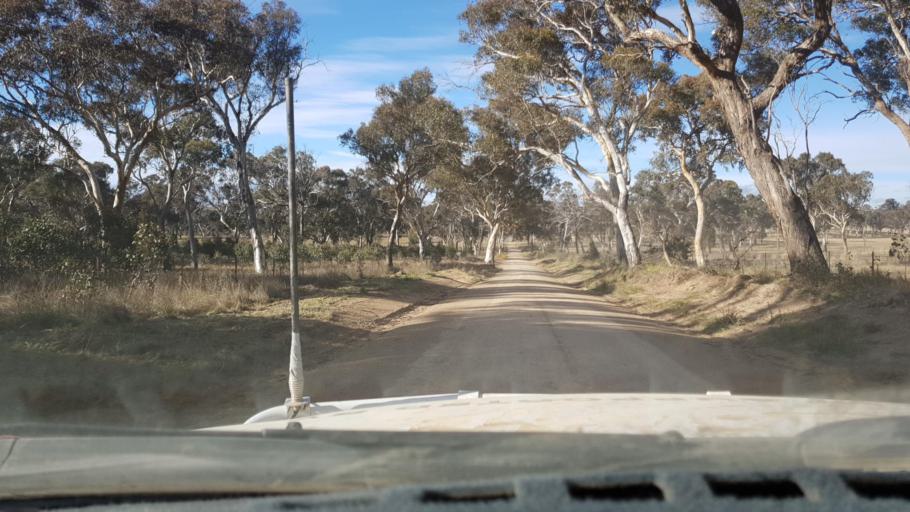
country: AU
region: New South Wales
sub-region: Armidale Dumaresq
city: Enmore
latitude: -30.7204
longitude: 151.5904
